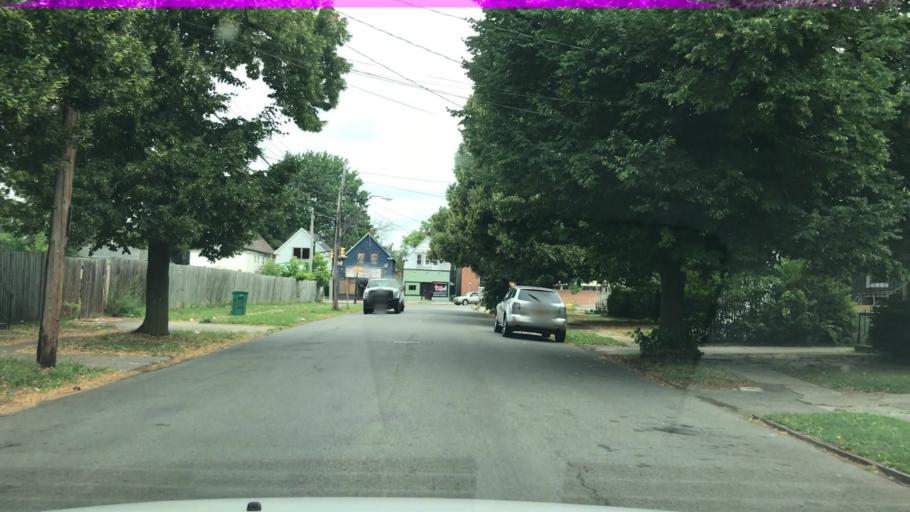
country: US
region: New York
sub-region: Erie County
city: Sloan
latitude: 42.9158
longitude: -78.8036
